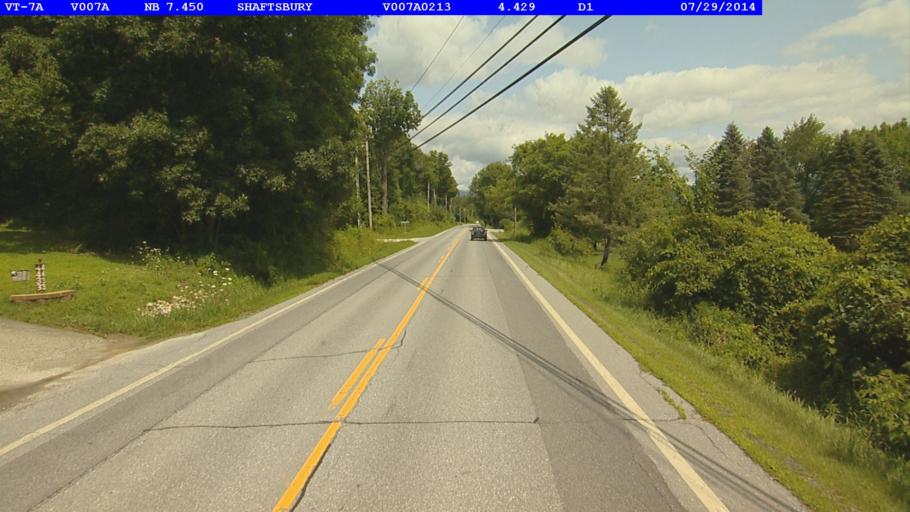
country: US
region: Vermont
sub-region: Bennington County
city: North Bennington
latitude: 42.9954
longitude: -73.2022
